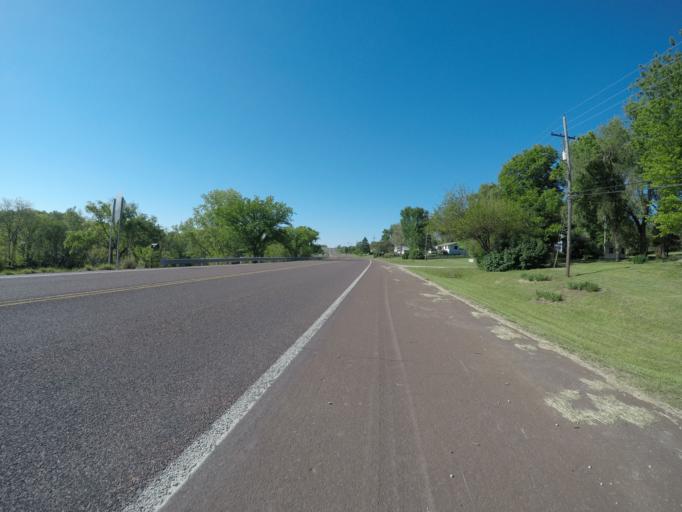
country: US
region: Kansas
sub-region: Douglas County
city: Lawrence
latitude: 39.0397
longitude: -95.3912
